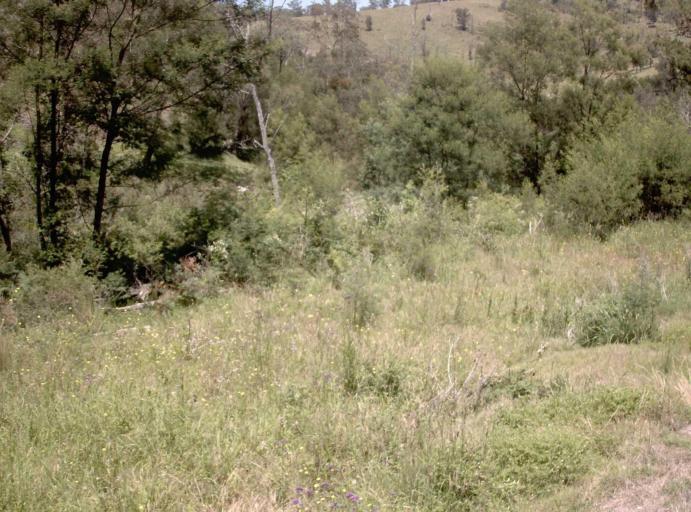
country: AU
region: Victoria
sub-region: East Gippsland
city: Bairnsdale
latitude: -37.5236
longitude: 147.8455
